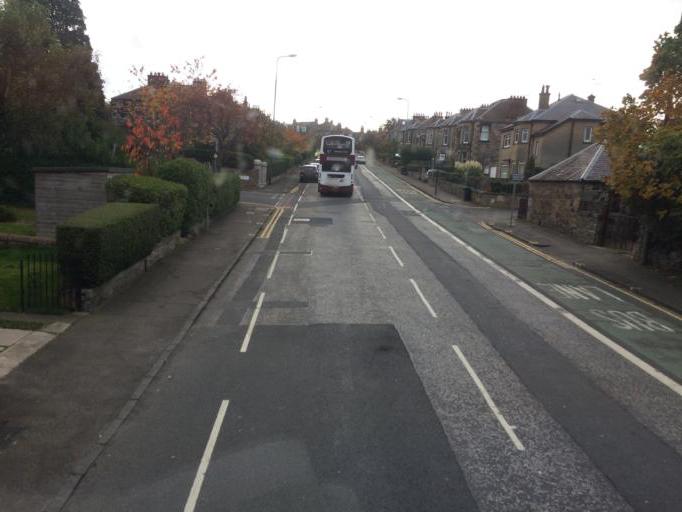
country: GB
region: Scotland
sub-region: Midlothian
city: Loanhead
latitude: 55.9187
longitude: -3.1673
